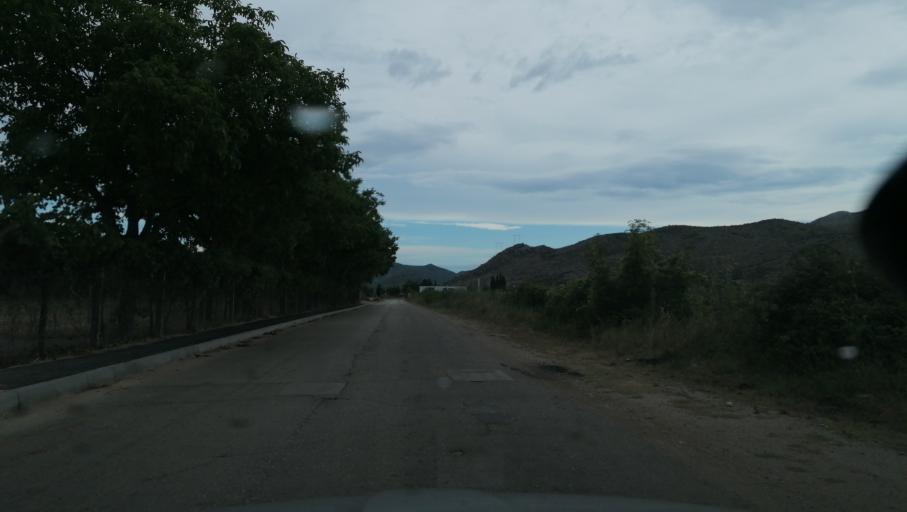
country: BA
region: Republika Srpska
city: Trebinje
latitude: 42.6745
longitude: 18.3303
